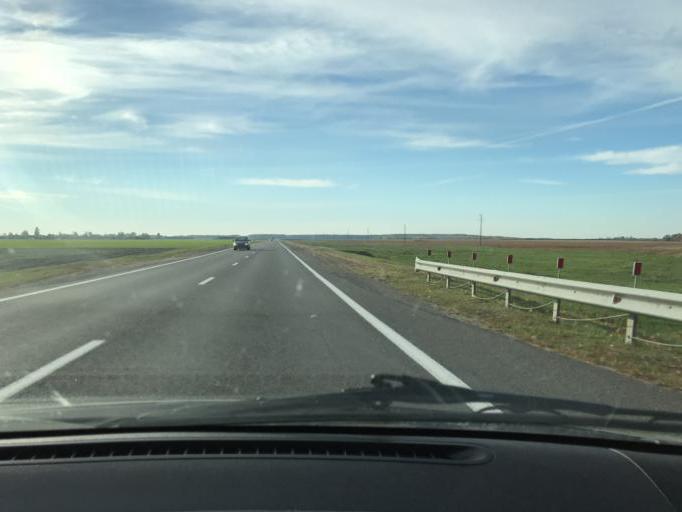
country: BY
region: Brest
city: Ivanava
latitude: 52.1560
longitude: 25.6655
